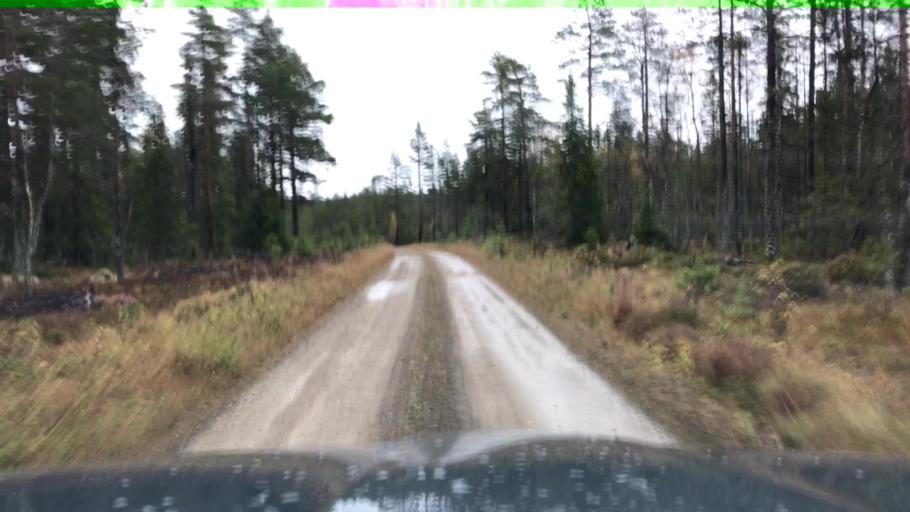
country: NO
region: Hedmark
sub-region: Trysil
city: Innbygda
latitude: 60.9248
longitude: 12.6348
